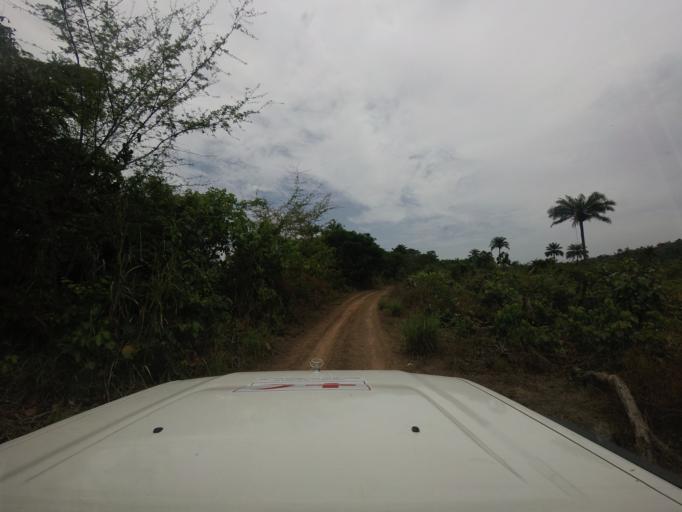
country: SL
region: Eastern Province
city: Buedu
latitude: 8.2336
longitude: -10.2932
